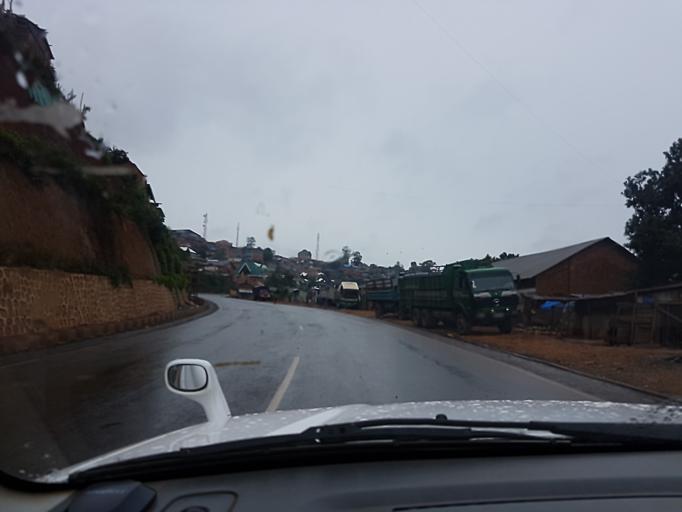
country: CD
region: South Kivu
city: Bukavu
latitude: -2.5131
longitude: 28.8549
